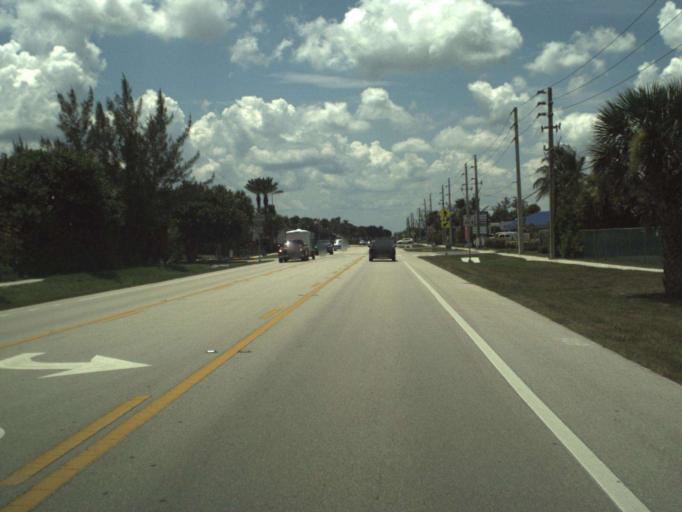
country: US
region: Florida
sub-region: Martin County
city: Jensen Beach
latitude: 27.2672
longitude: -80.2033
